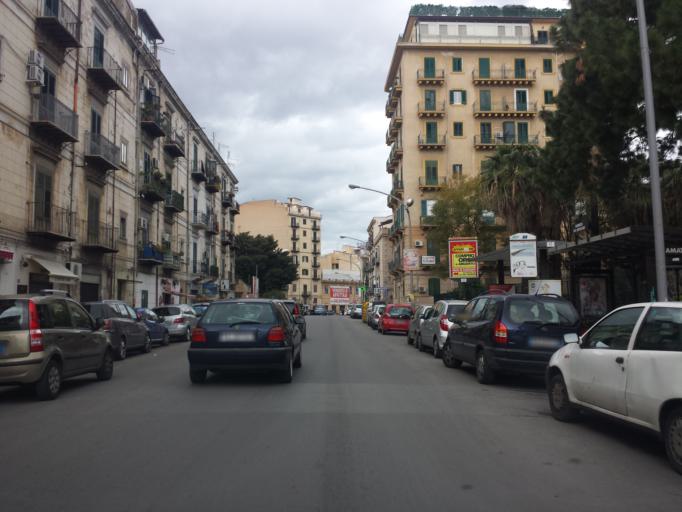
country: IT
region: Sicily
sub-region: Palermo
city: Palermo
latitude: 38.1166
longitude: 13.3520
